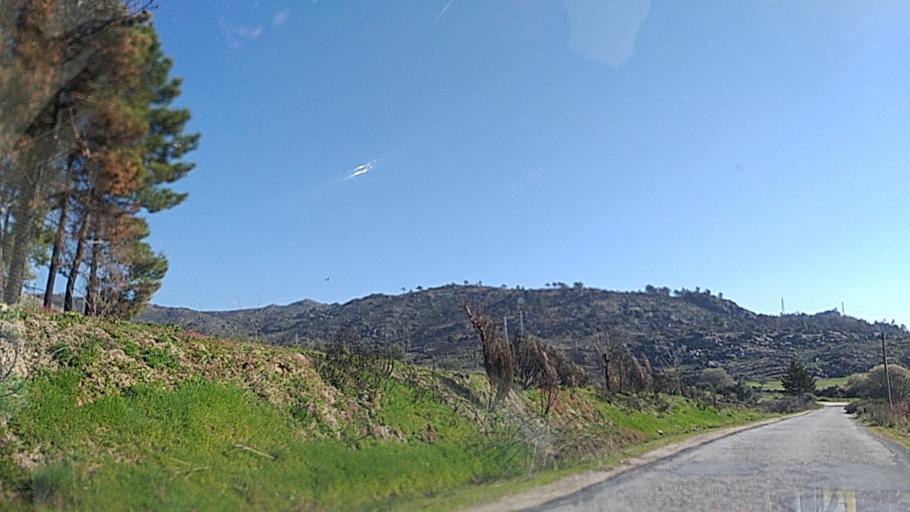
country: PT
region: Guarda
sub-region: Celorico da Beira
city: Celorico da Beira
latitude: 40.6907
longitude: -7.4245
